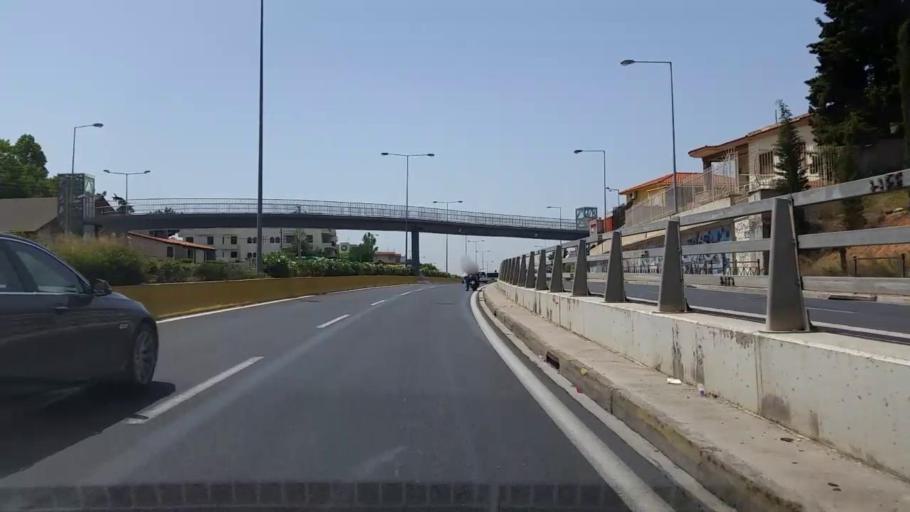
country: GR
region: Attica
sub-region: Nomarchia Athinas
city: Agia Paraskevi
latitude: 38.0111
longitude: 23.8398
